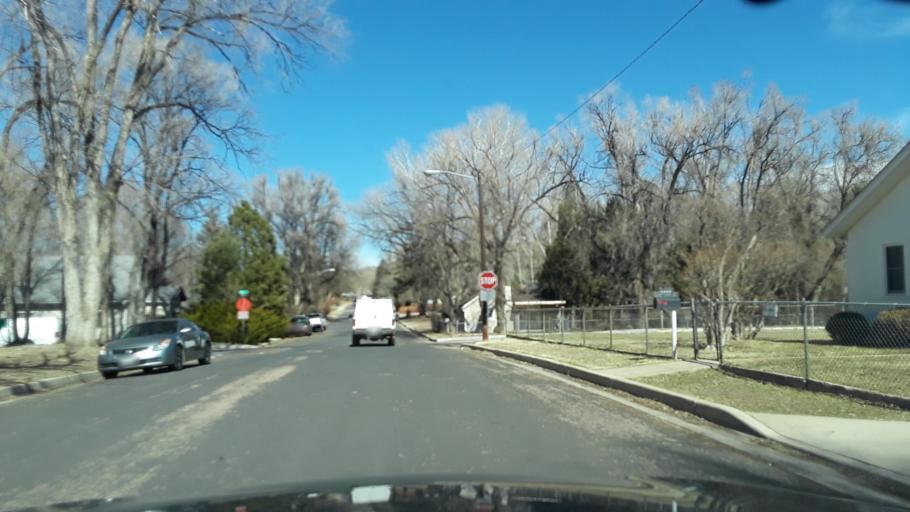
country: US
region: Colorado
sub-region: El Paso County
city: Colorado Springs
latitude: 38.8770
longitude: -104.8055
